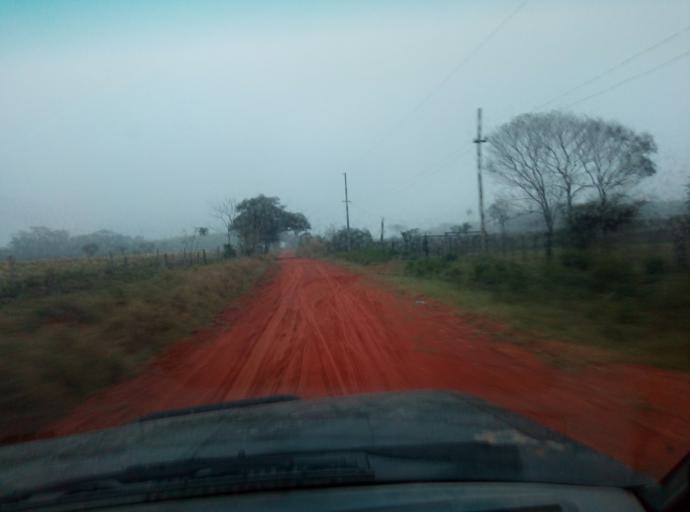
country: PY
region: Caaguazu
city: Doctor Cecilio Baez
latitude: -25.1558
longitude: -56.2828
